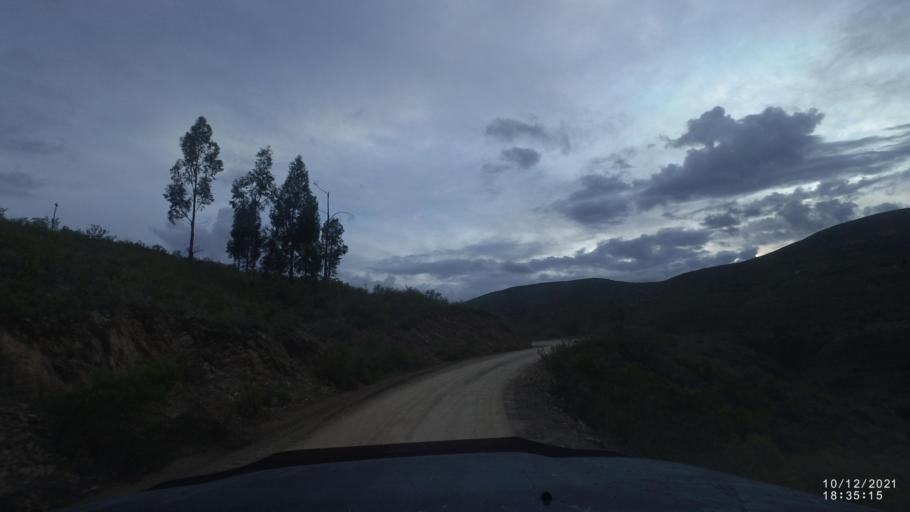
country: BO
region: Cochabamba
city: Tarata
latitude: -17.8269
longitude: -65.9906
